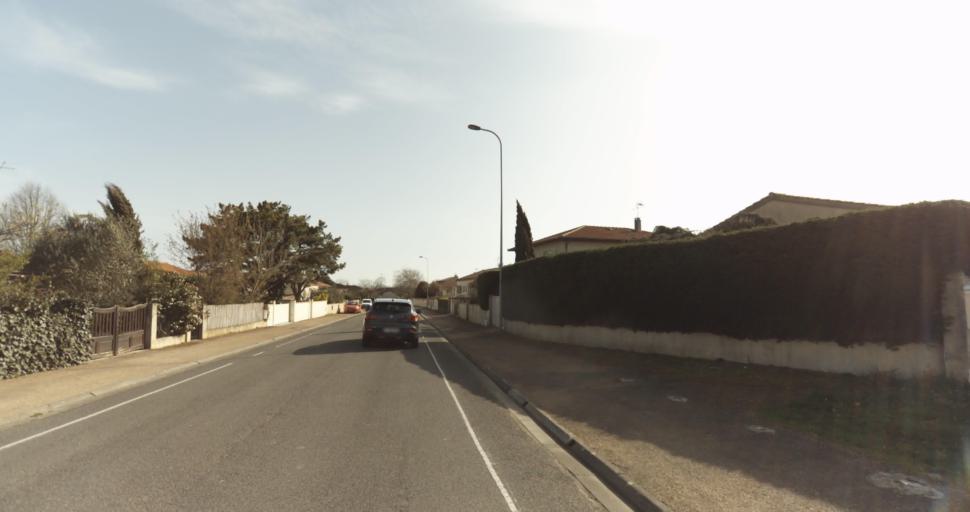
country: FR
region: Midi-Pyrenees
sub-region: Departement du Tarn
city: Saint-Sulpice-la-Pointe
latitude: 43.7696
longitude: 1.6954
